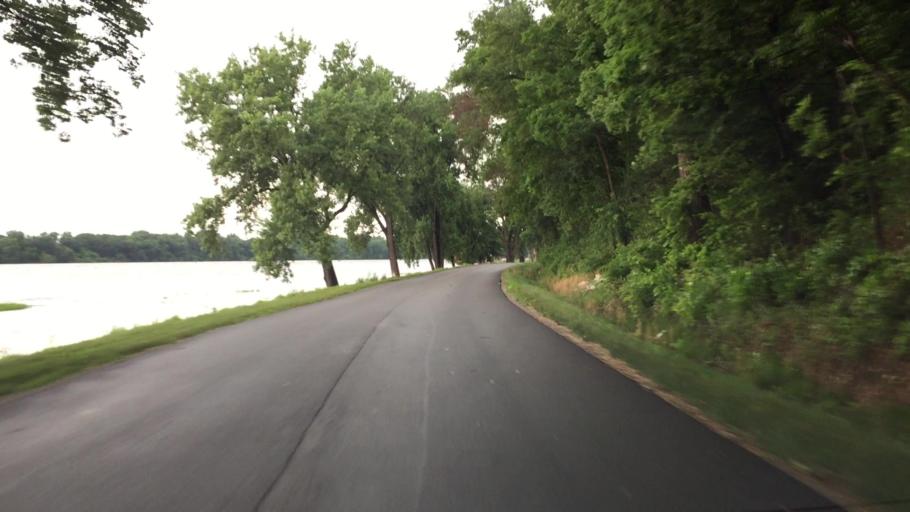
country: US
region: Illinois
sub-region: Hancock County
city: Warsaw
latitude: 40.3582
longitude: -91.4444
